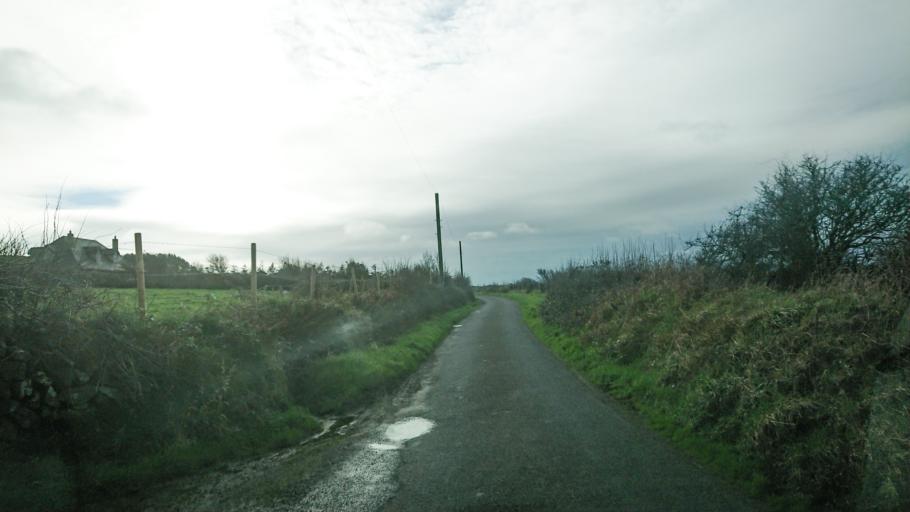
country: IE
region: Munster
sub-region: Waterford
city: Tra Mhor
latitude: 52.1496
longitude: -7.1925
